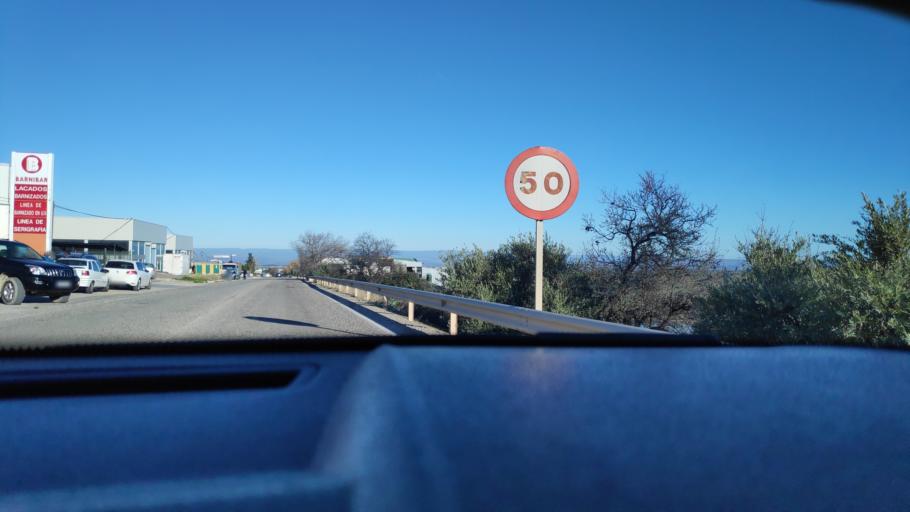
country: ES
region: Andalusia
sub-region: Provincia de Jaen
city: Mancha Real
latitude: 37.7992
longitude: -3.6094
